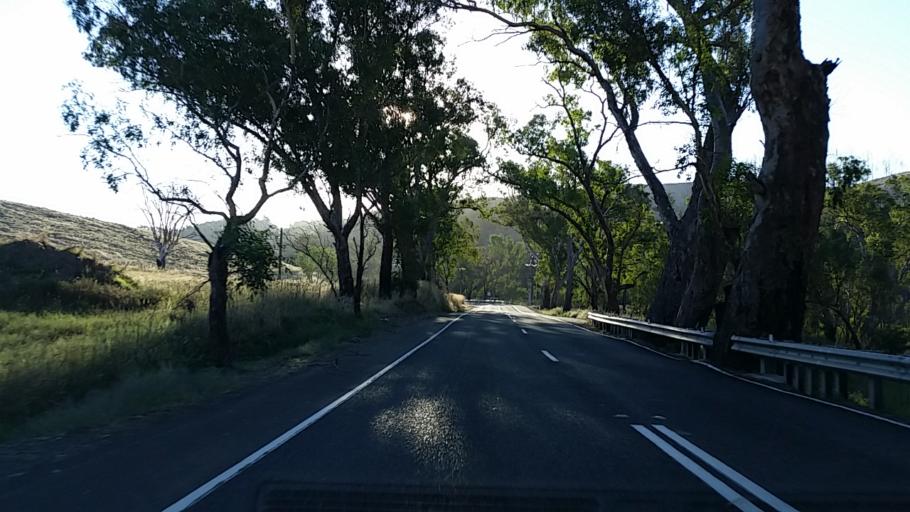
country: AU
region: South Australia
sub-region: Adelaide Hills
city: Gumeracha
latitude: -34.8200
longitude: 138.8596
